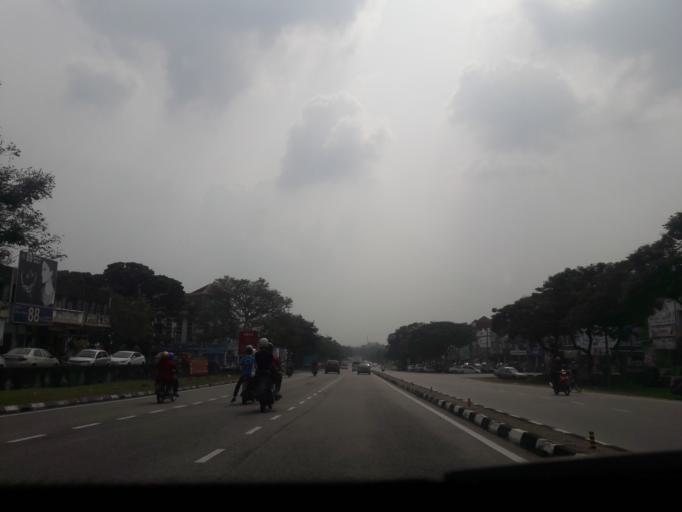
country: MY
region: Kedah
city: Kulim
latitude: 5.3747
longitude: 100.5368
